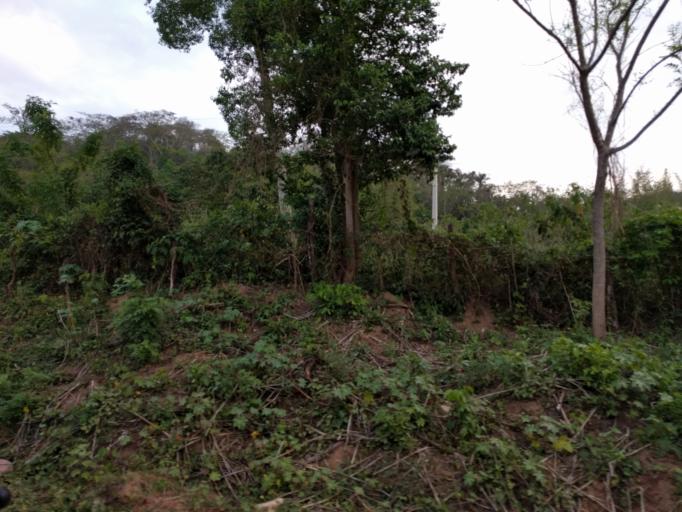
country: BO
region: Santa Cruz
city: Santa Rita
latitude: -17.9324
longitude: -63.3816
